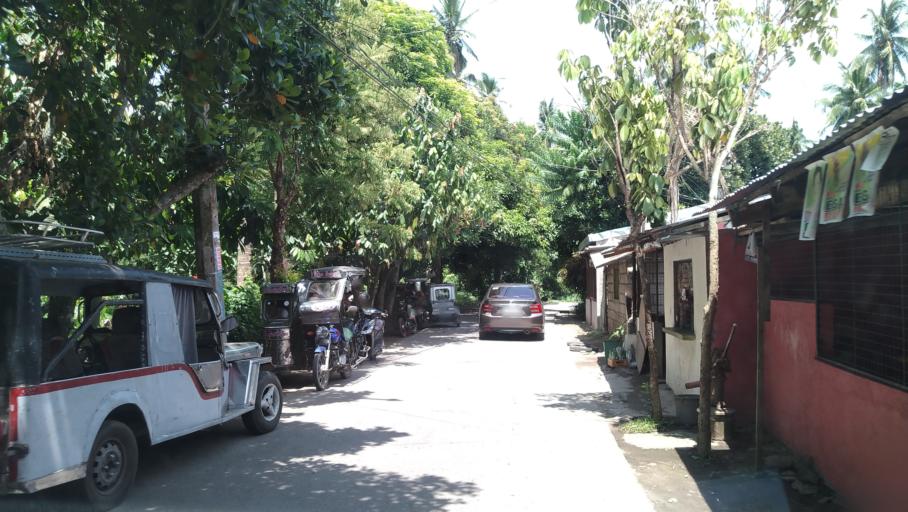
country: PH
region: Calabarzon
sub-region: Province of Laguna
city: Cabanbanan
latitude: 14.2432
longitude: 121.4054
